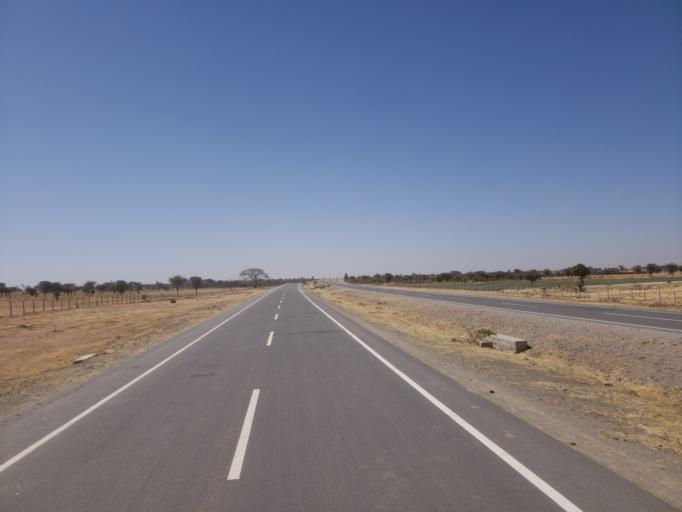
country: ET
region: Oromiya
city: Ziway
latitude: 8.2632
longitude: 38.9021
